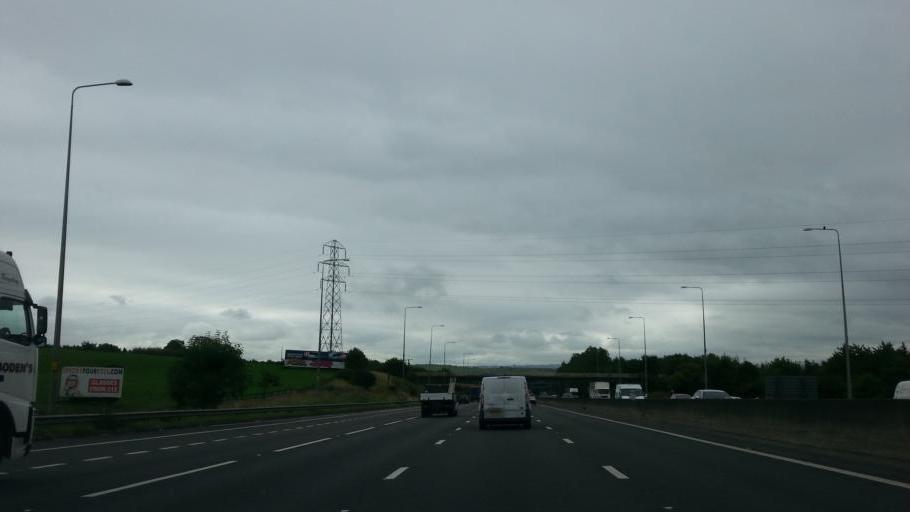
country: GB
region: England
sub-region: Kirklees
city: Cleckheaton
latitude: 53.7092
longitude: -1.7443
